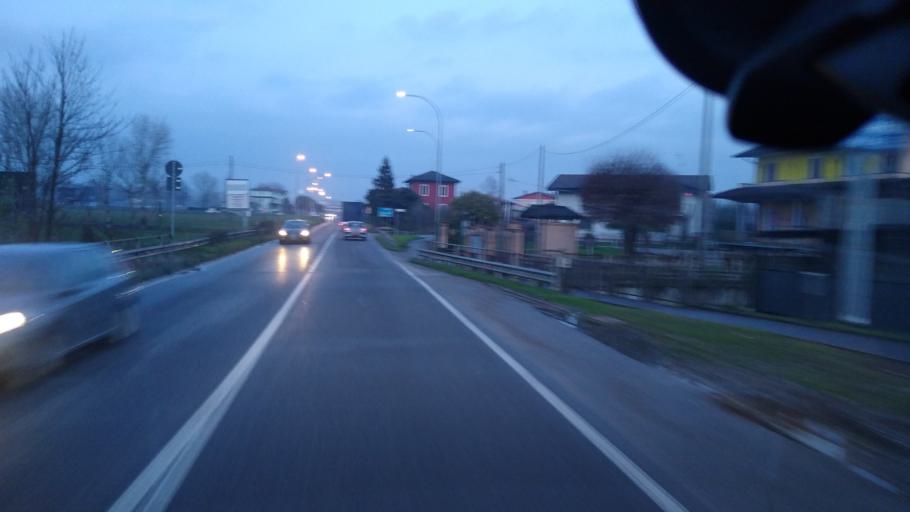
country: IT
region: Lombardy
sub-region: Provincia di Bergamo
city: Mozzanica
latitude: 45.4796
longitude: 9.6943
